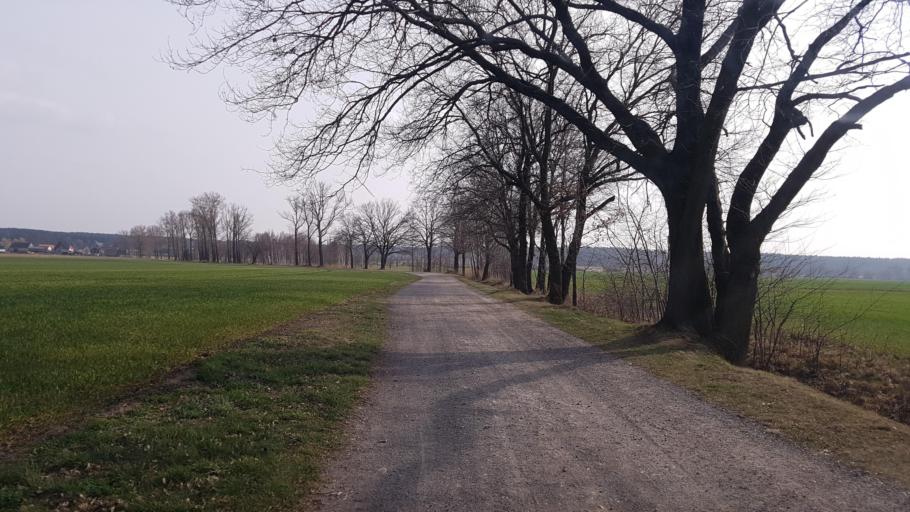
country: DE
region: Brandenburg
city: Merzdorf
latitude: 51.4136
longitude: 13.5267
